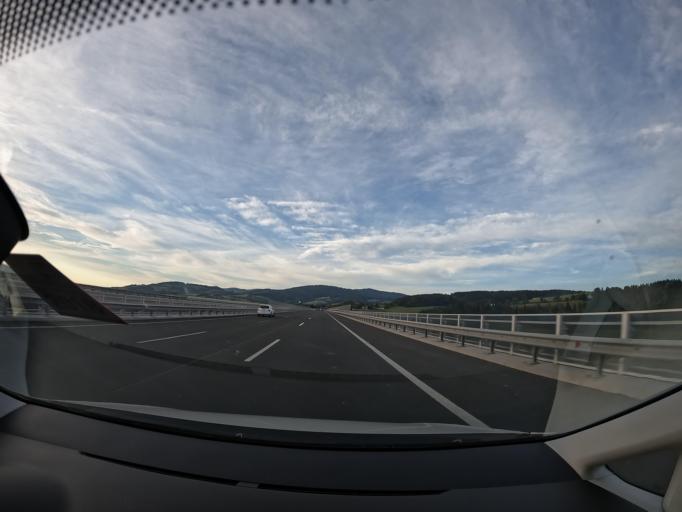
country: AT
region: Carinthia
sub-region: Politischer Bezirk Wolfsberg
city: Bad Sankt Leonhard im Lavanttal
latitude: 46.9258
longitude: 14.8229
